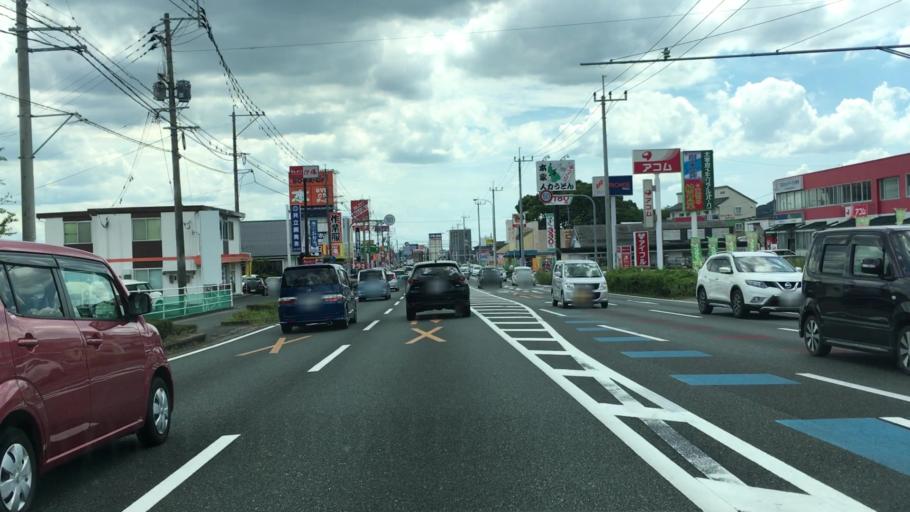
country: JP
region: Saga Prefecture
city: Tosu
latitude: 33.3843
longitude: 130.4994
